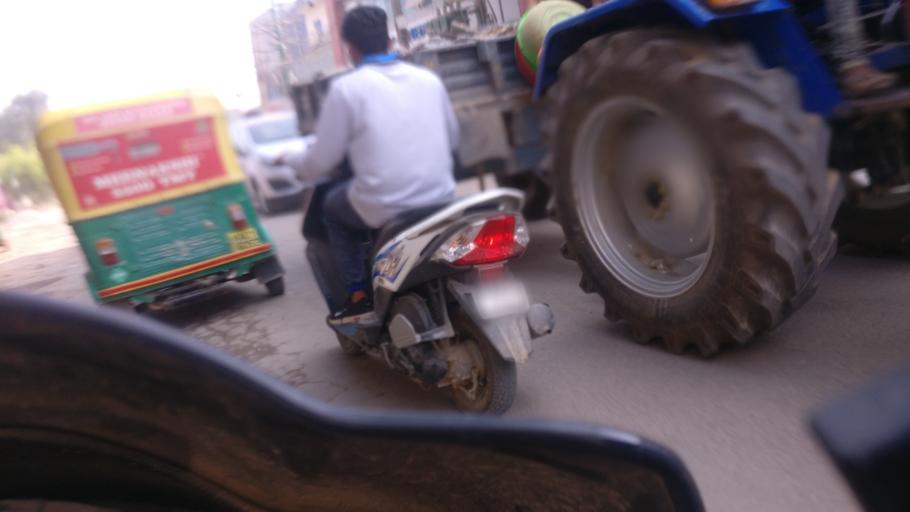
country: IN
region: Karnataka
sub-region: Bangalore Urban
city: Bangalore
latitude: 12.8776
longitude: 77.6717
